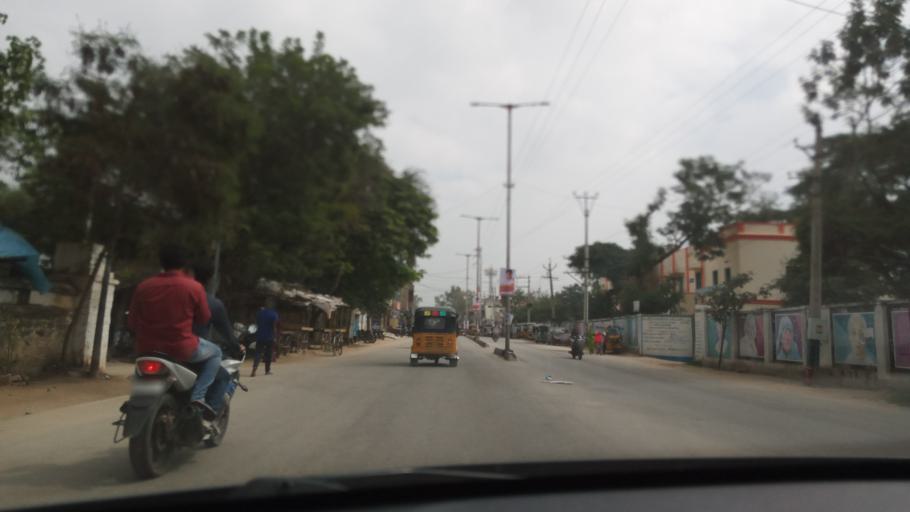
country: IN
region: Andhra Pradesh
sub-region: Chittoor
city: Madanapalle
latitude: 13.5558
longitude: 78.4981
